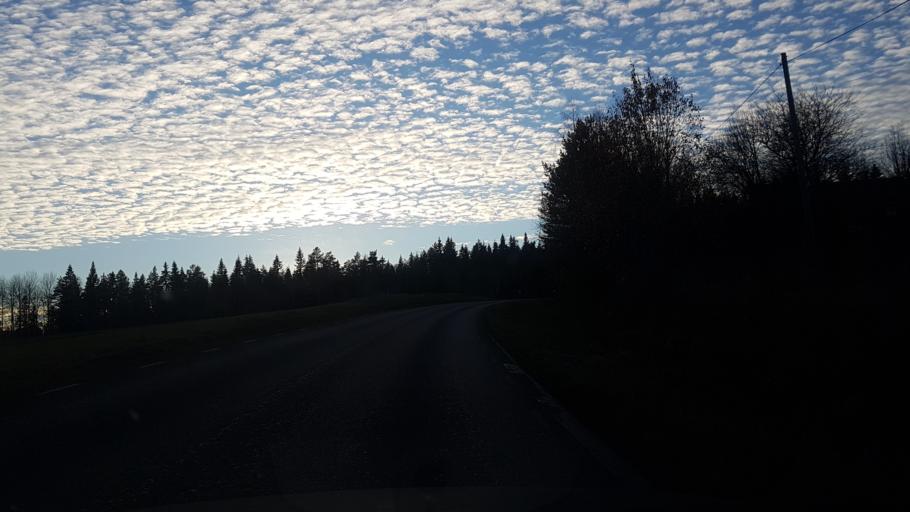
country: SE
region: Dalarna
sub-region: Leksand Municipality
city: Smedby
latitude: 60.7302
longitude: 15.1402
